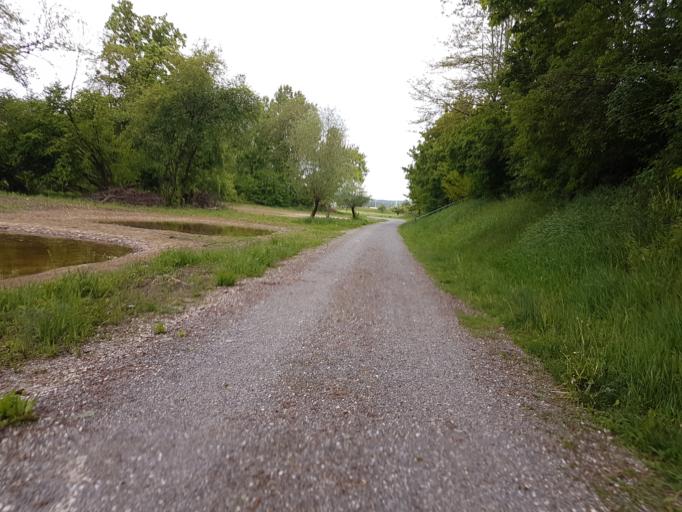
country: CH
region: Aargau
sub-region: Bezirk Brugg
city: Lauffohr (Brugg)
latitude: 47.5012
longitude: 8.2336
